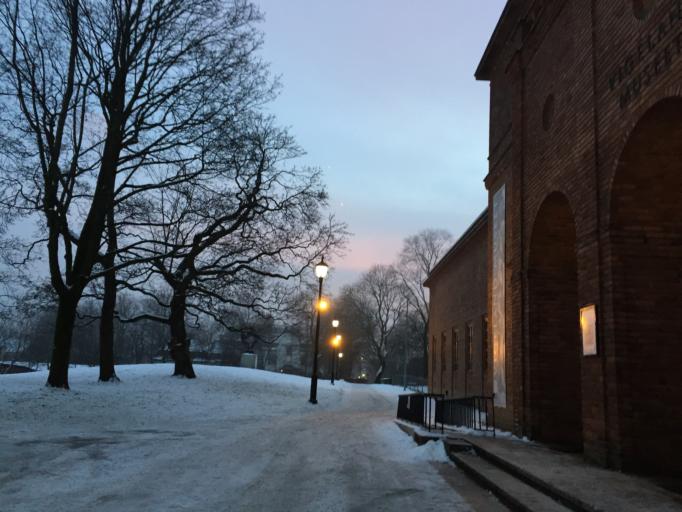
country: NO
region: Oslo
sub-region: Oslo
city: Sjolyststranda
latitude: 59.9229
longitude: 10.7006
